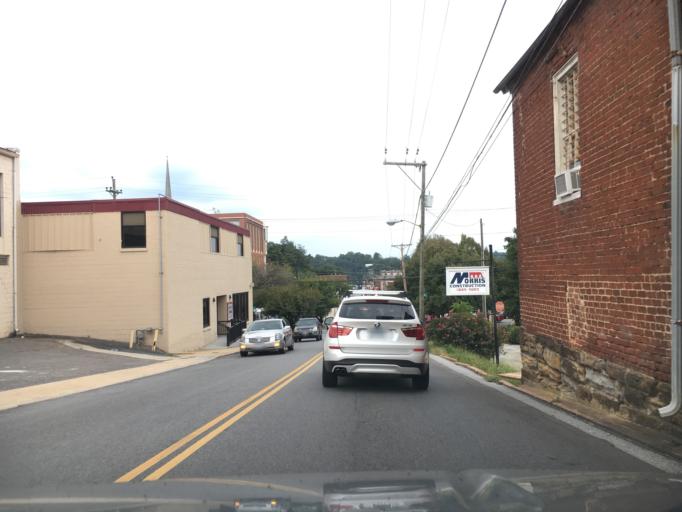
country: US
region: Virginia
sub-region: City of Lynchburg
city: Lynchburg
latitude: 37.4100
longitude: -79.1443
